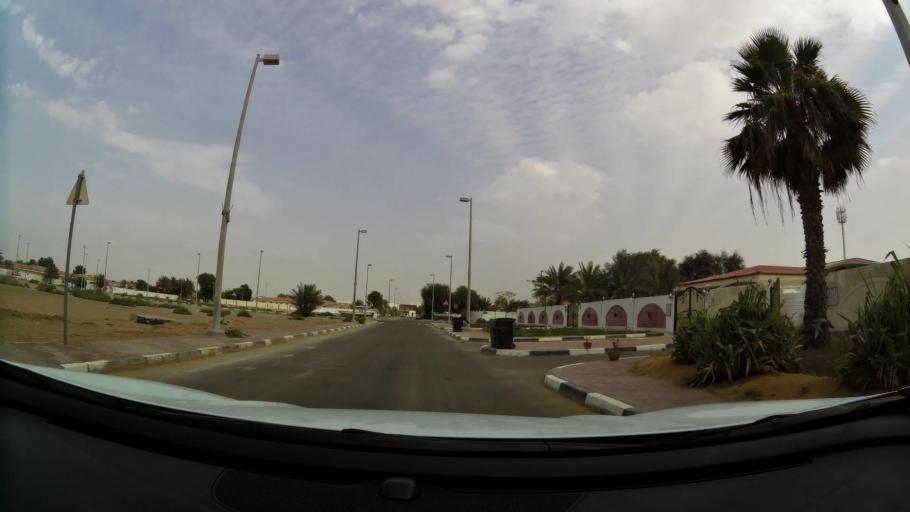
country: AE
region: Abu Dhabi
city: Abu Dhabi
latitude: 24.5187
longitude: 54.6865
